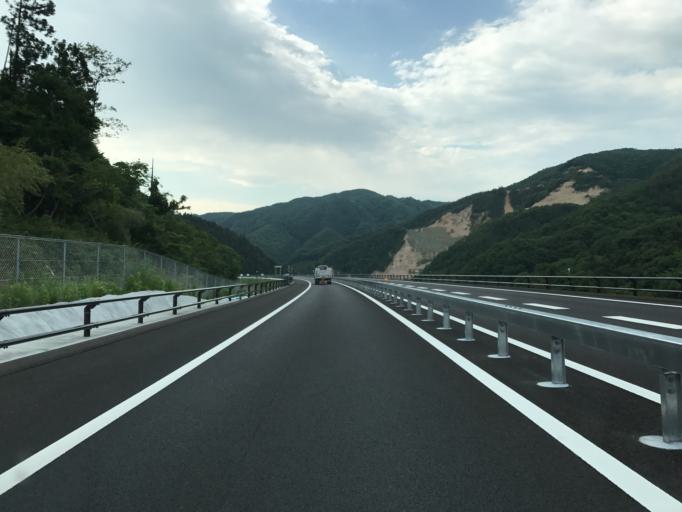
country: JP
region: Miyagi
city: Marumori
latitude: 37.7875
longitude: 140.7907
